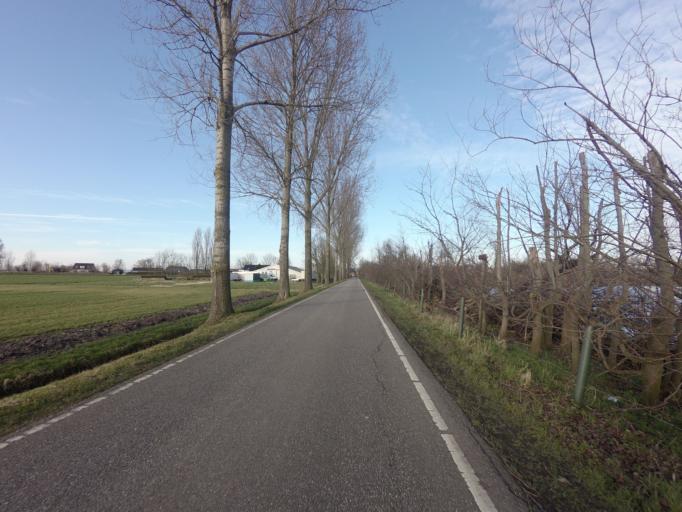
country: NL
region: South Holland
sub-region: Bodegraven-Reeuwijk
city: Bodegraven
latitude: 52.0830
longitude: 4.7906
